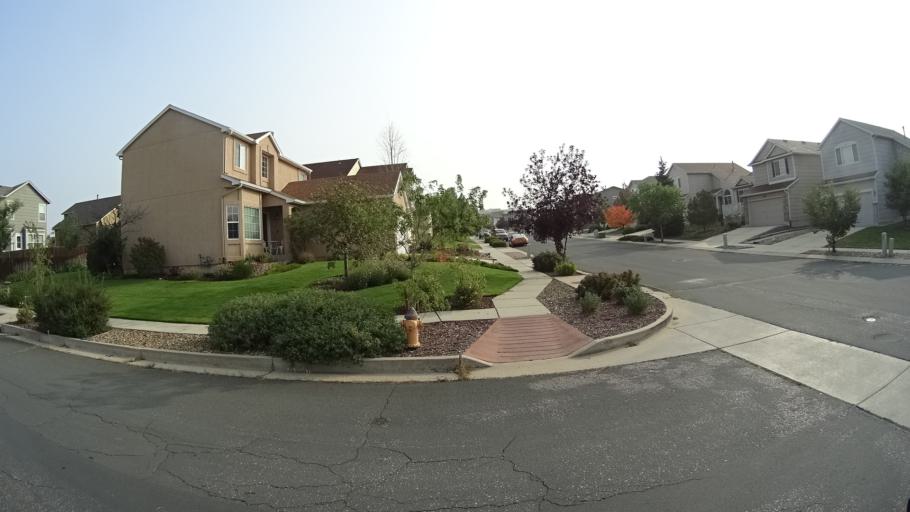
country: US
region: Colorado
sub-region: El Paso County
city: Cimarron Hills
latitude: 38.9343
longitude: -104.7271
